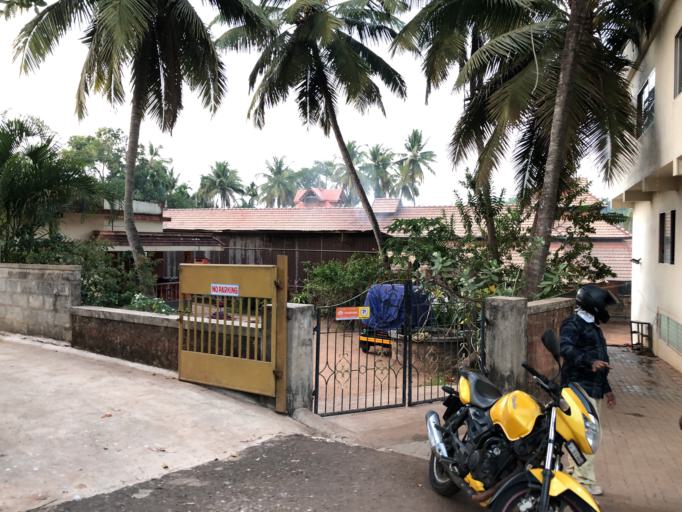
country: IN
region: Karnataka
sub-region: Dakshina Kannada
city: Mangalore
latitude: 12.8758
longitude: 74.8762
